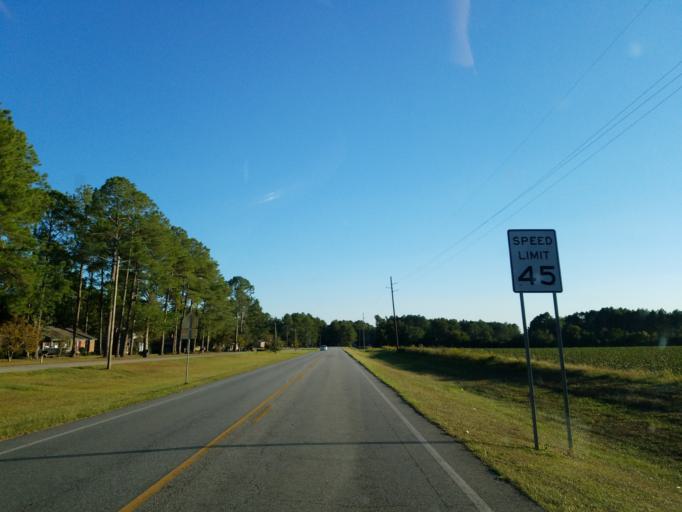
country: US
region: Georgia
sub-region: Worth County
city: Sylvester
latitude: 31.5439
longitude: -83.8431
